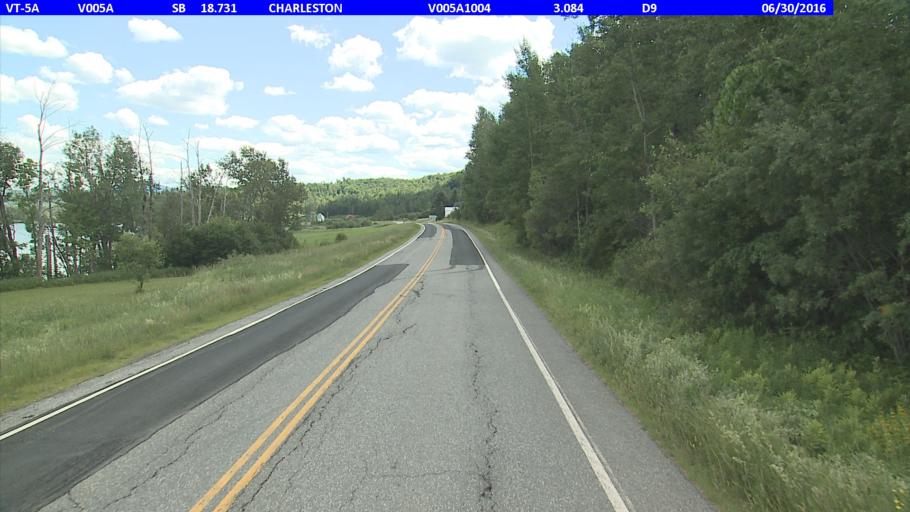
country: US
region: Vermont
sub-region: Orleans County
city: Newport
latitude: 44.8748
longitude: -72.0610
